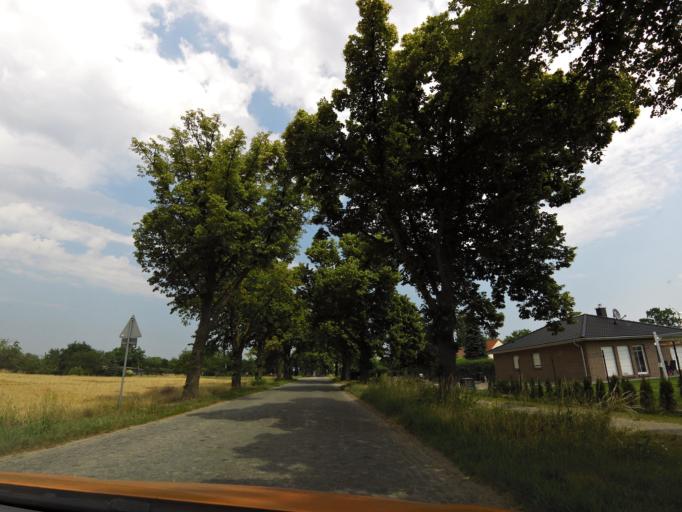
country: DE
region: Brandenburg
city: Nauen
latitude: 52.5808
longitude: 12.8746
